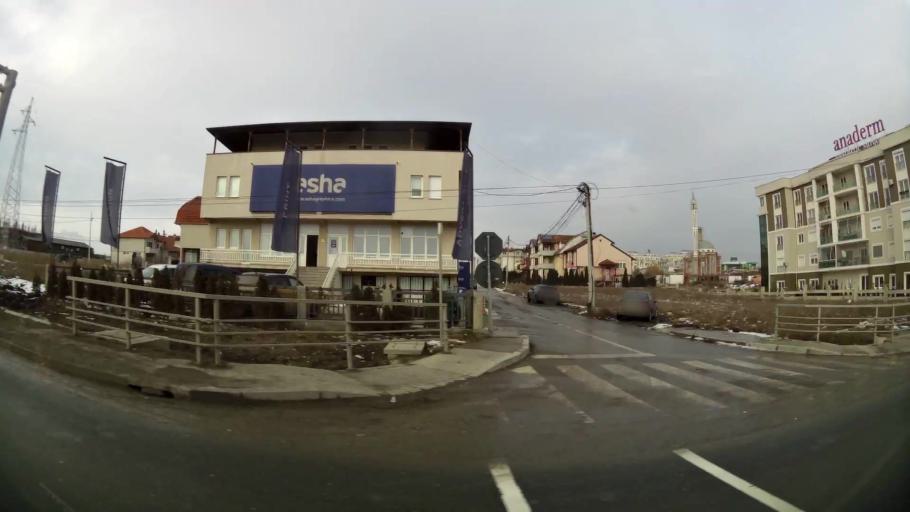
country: XK
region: Pristina
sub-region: Komuna e Prishtines
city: Pristina
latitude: 42.6313
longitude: 21.1474
